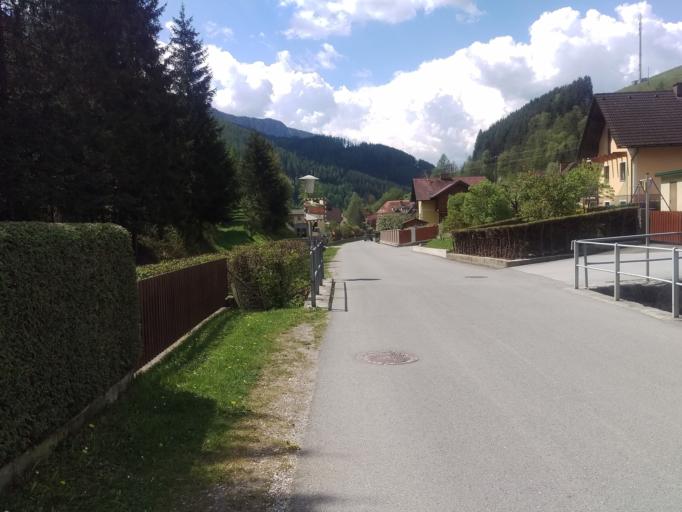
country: AT
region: Styria
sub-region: Politischer Bezirk Bruck-Muerzzuschlag
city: Allerheiligen im Muerztal
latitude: 47.3958
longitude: 15.4331
